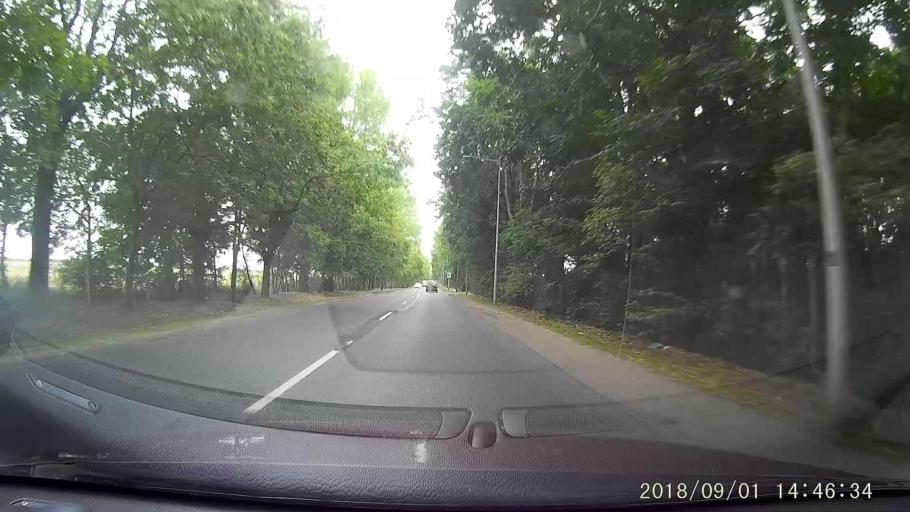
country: PL
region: Lubusz
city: Gorzow Wielkopolski
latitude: 52.7418
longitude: 15.1753
